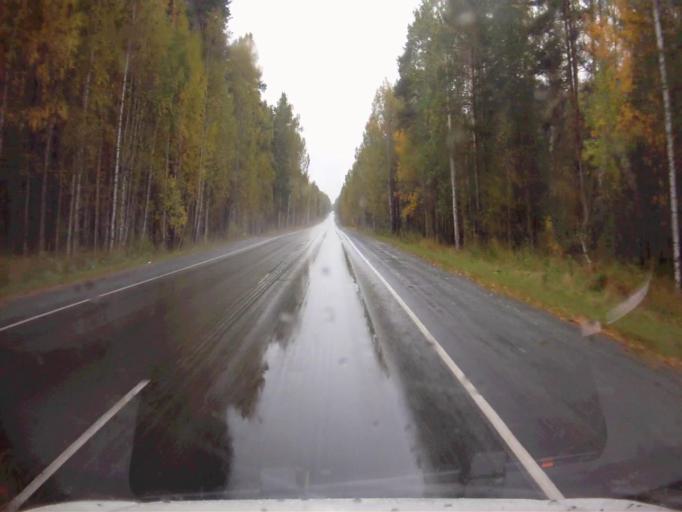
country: RU
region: Chelyabinsk
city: Tayginka
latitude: 55.5780
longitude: 60.6443
